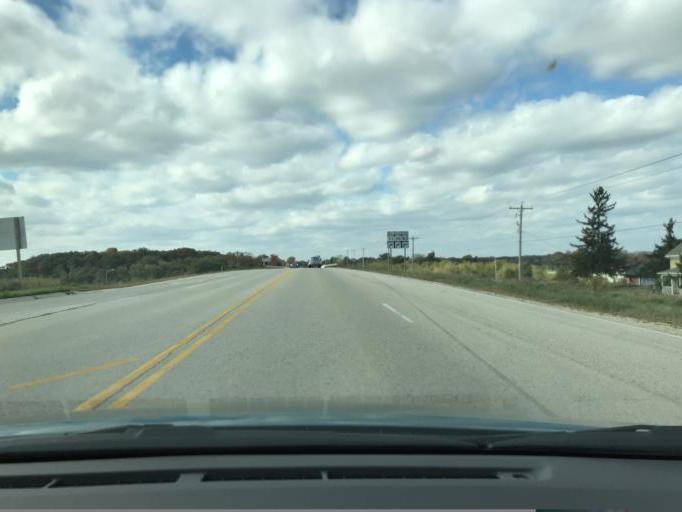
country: US
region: Wisconsin
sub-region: Racine County
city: Browns Lake
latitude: 42.6627
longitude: -88.2417
